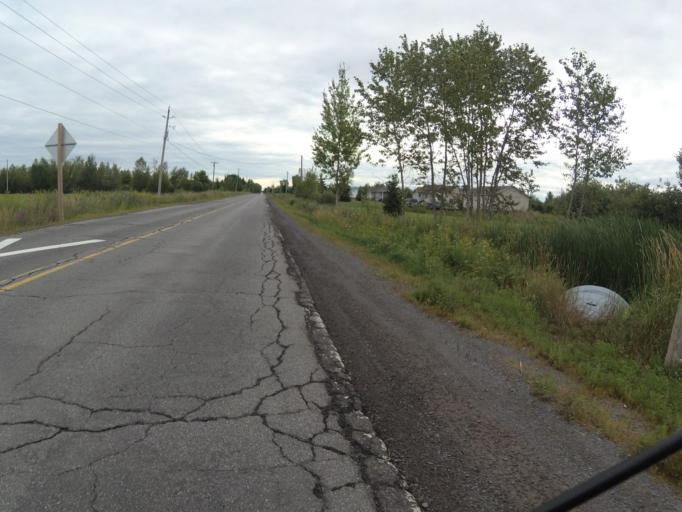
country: CA
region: Ontario
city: Bourget
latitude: 45.3433
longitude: -75.3127
